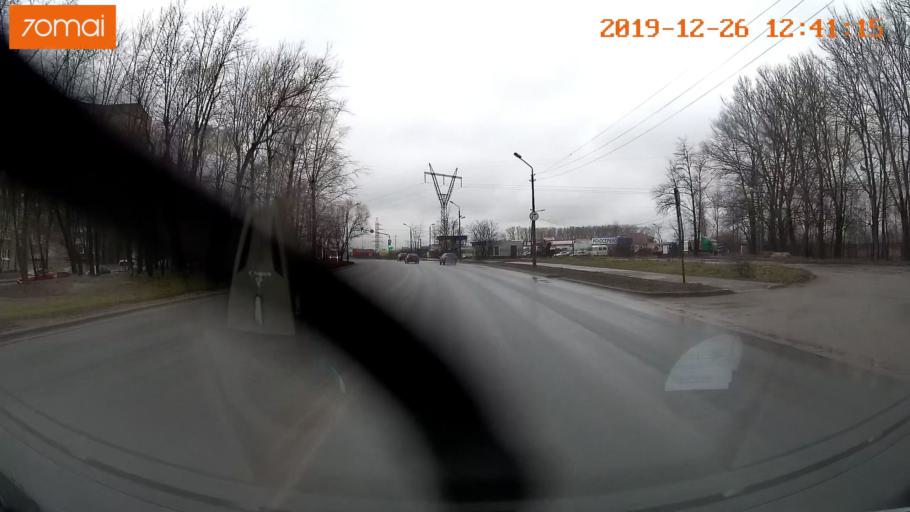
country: RU
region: Vologda
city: Tonshalovo
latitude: 59.1481
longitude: 37.9643
